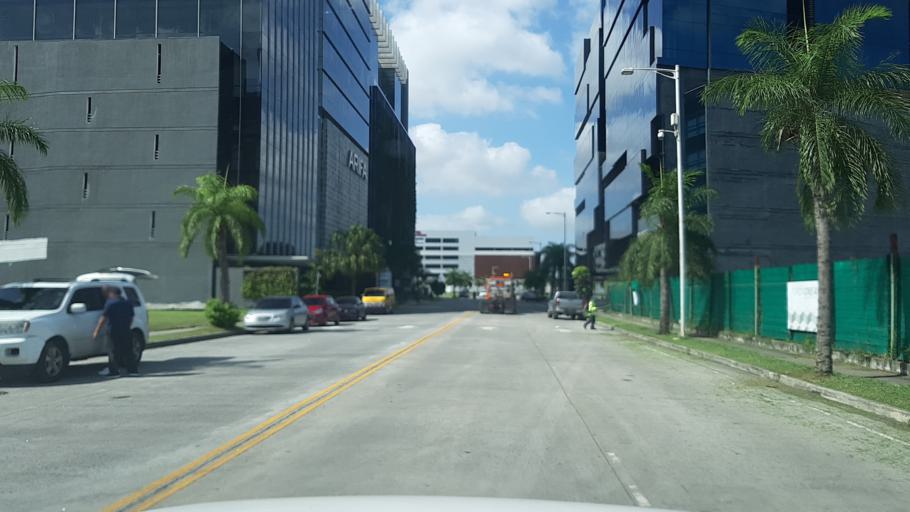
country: PA
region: Panama
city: San Miguelito
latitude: 9.0285
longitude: -79.4614
